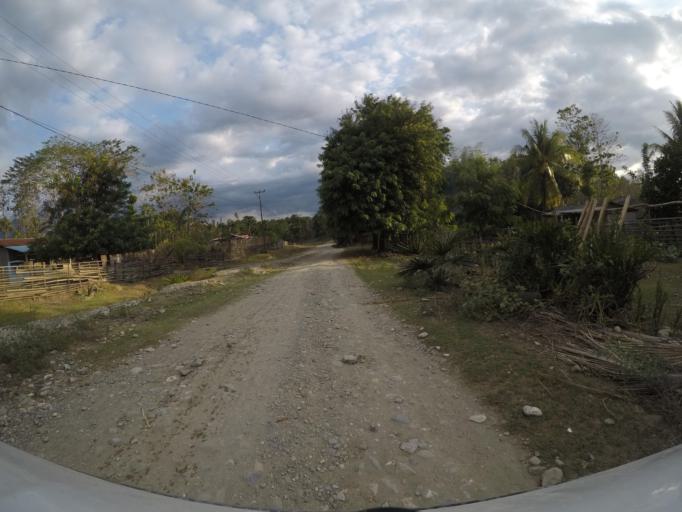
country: TL
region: Bobonaro
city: Maliana
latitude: -8.8629
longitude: 125.2162
